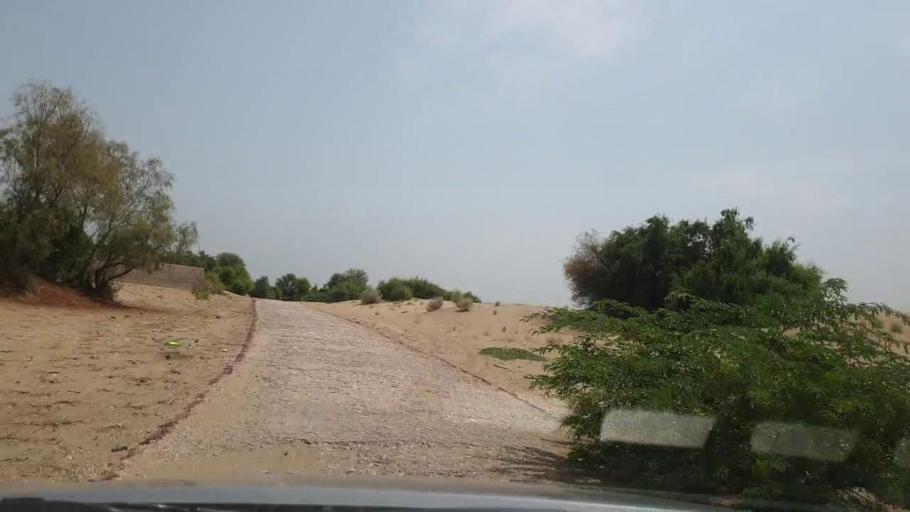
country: PK
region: Sindh
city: Pano Aqil
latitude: 27.5812
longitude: 69.1707
